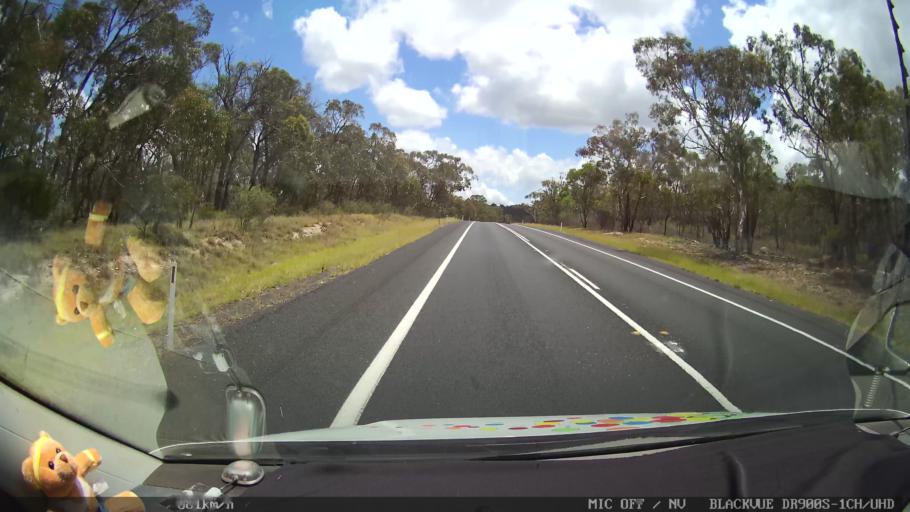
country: AU
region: New South Wales
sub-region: Glen Innes Severn
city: Glen Innes
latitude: -29.3587
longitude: 151.8982
